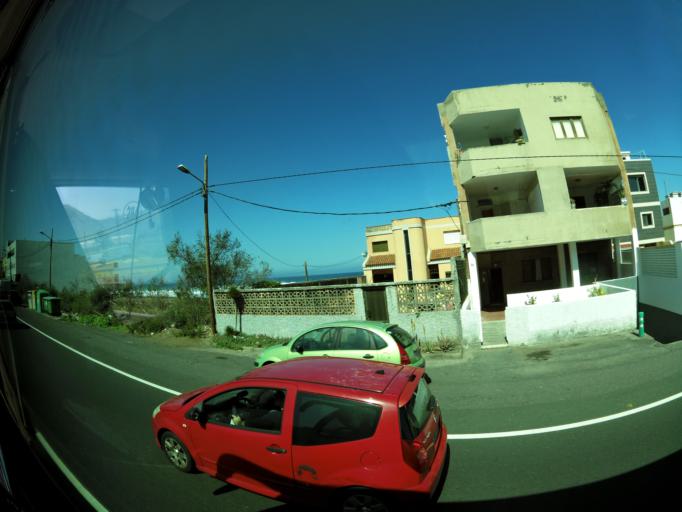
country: ES
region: Canary Islands
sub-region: Provincia de Las Palmas
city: Firgas
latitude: 28.1453
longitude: -15.5548
